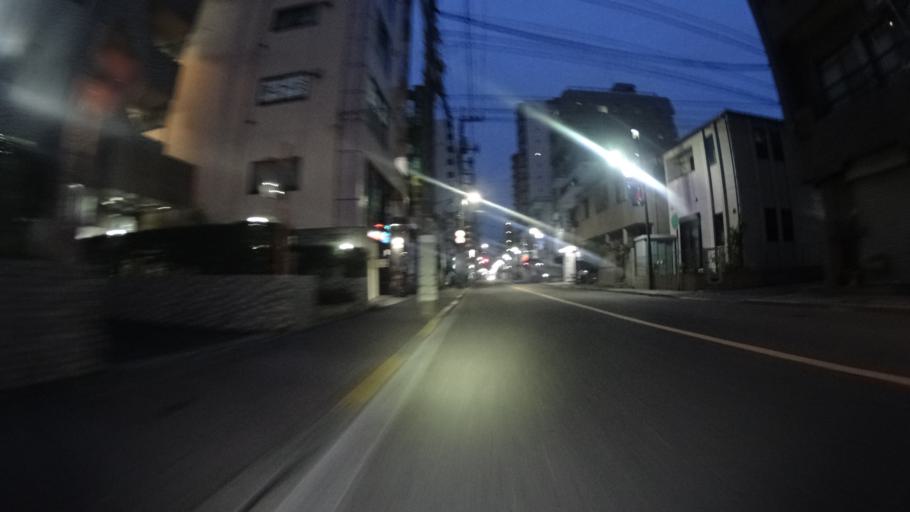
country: JP
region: Tokyo
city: Kokubunji
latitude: 35.6695
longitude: 139.4911
